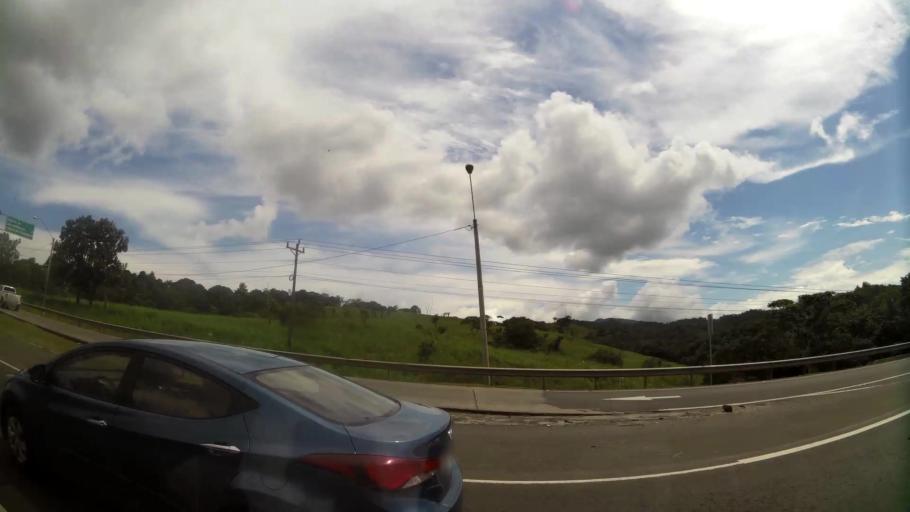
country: PA
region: Panama
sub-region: Distrito Arraijan
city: Arraijan
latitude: 8.9490
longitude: -79.6633
